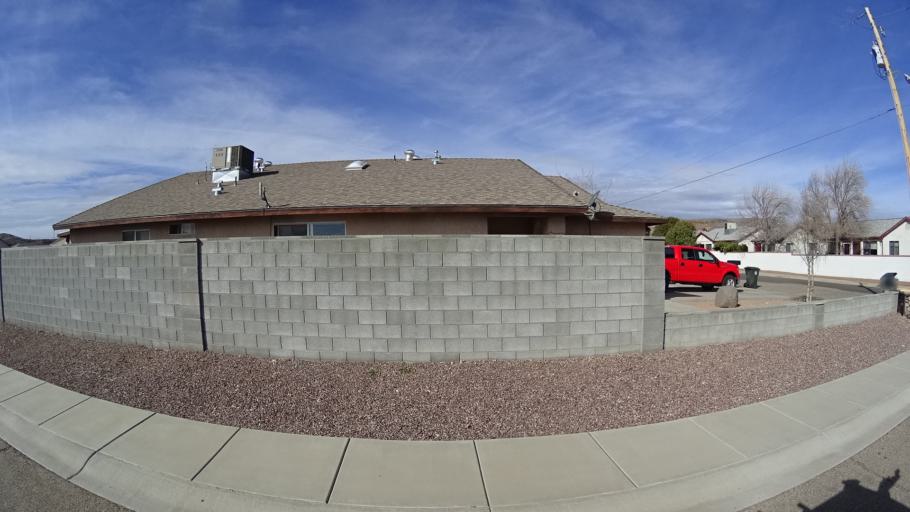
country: US
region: Arizona
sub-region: Mohave County
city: Kingman
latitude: 35.2205
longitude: -114.0424
